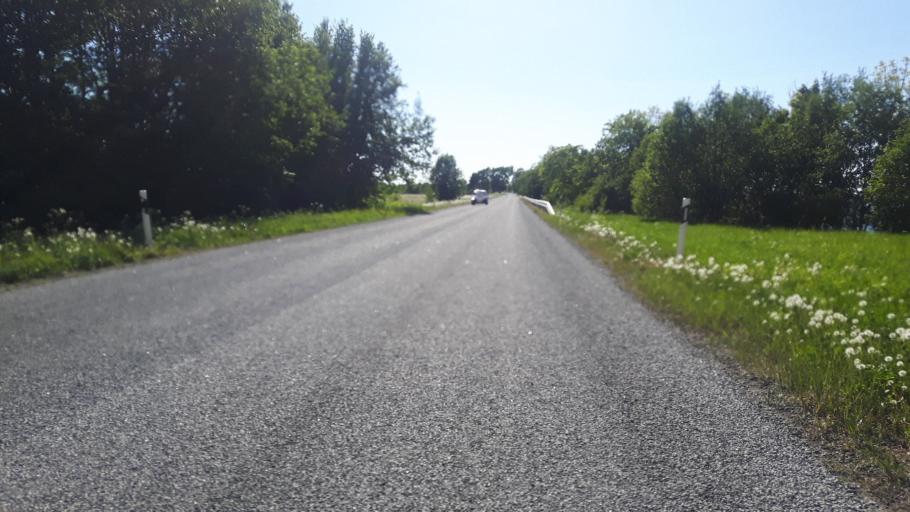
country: EE
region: Ida-Virumaa
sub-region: Kohtla-Jaerve linn
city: Kohtla-Jarve
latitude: 59.4431
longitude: 27.3195
